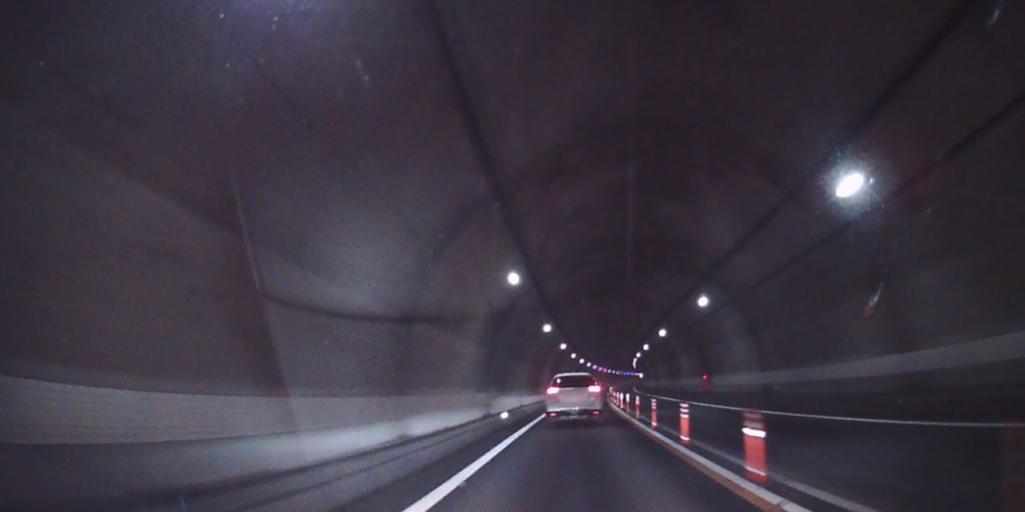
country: JP
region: Hokkaido
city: Niseko Town
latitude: 42.5915
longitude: 140.6821
